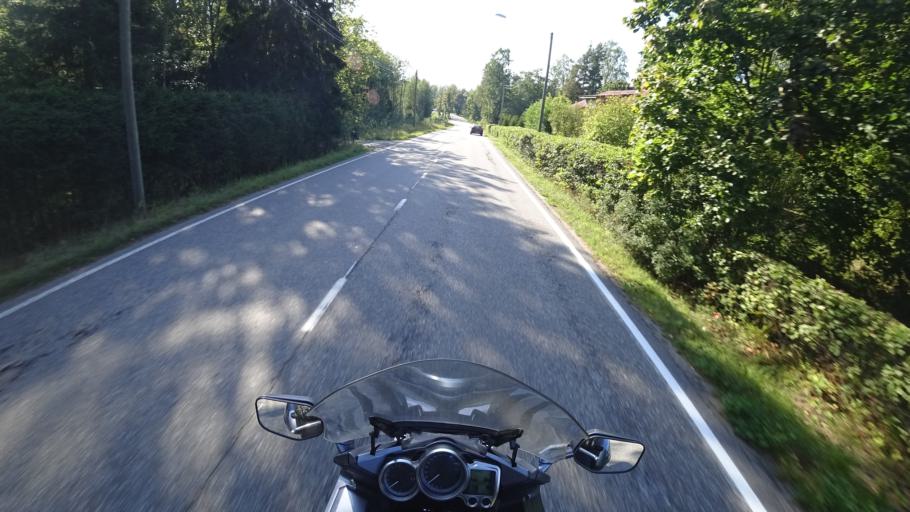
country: FI
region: Uusimaa
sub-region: Helsinki
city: Sammatti
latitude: 60.3172
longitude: 23.8371
